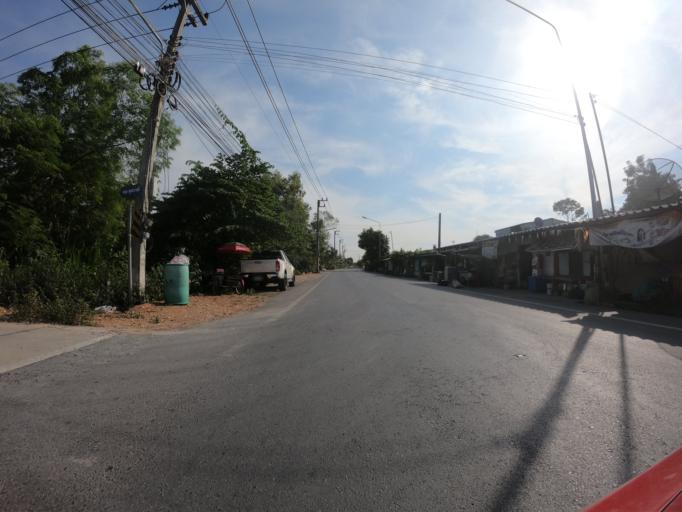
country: TH
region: Pathum Thani
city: Thanyaburi
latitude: 13.9834
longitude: 100.7294
